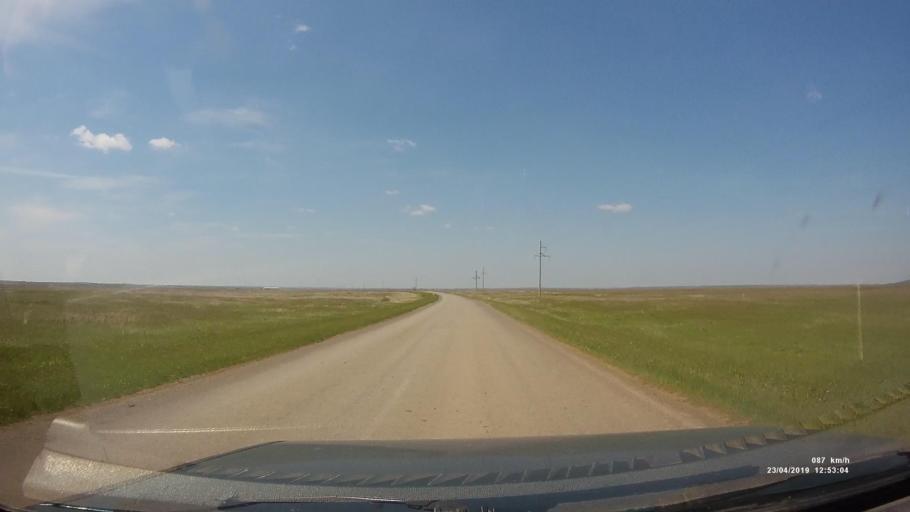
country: RU
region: Kalmykiya
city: Yashalta
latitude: 46.5707
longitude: 42.6013
